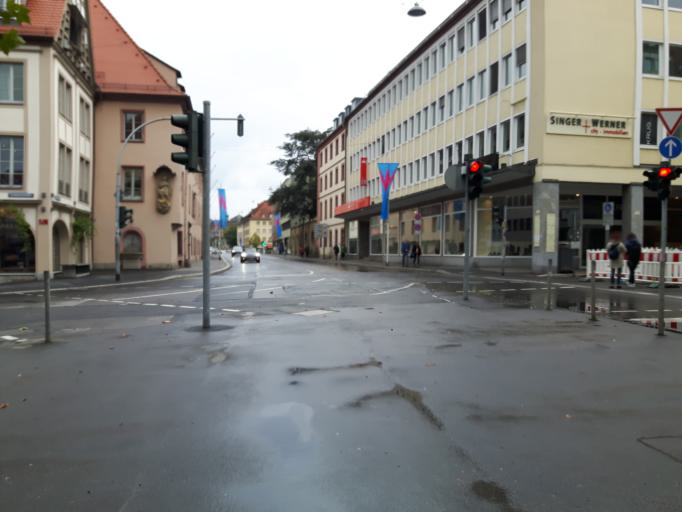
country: DE
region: Bavaria
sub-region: Regierungsbezirk Unterfranken
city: Wuerzburg
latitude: 49.7962
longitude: 9.9344
